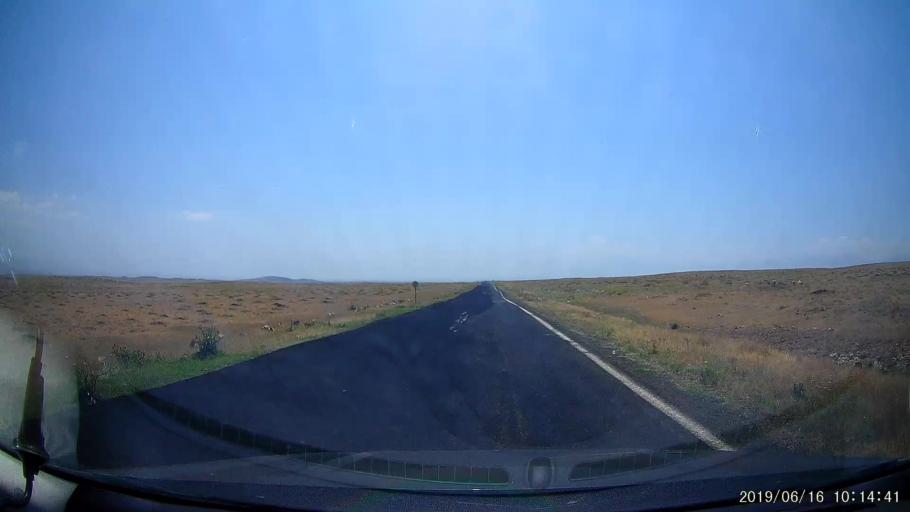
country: TR
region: Igdir
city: Tuzluca
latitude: 40.1827
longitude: 43.6677
